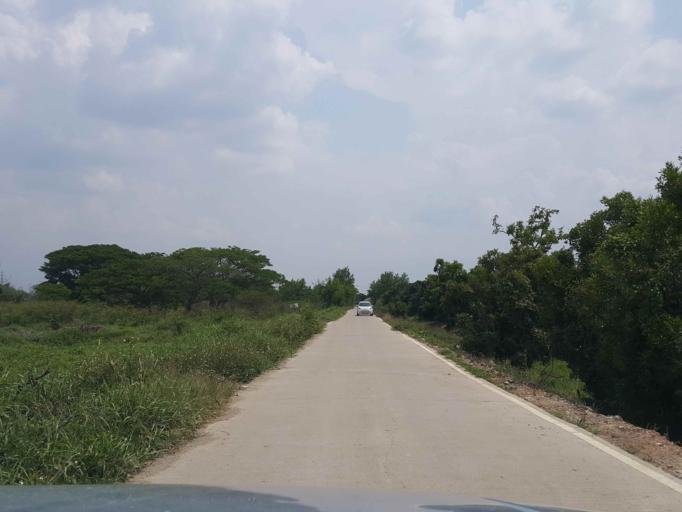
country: TH
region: Chiang Mai
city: Saraphi
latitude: 18.6701
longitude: 99.0217
